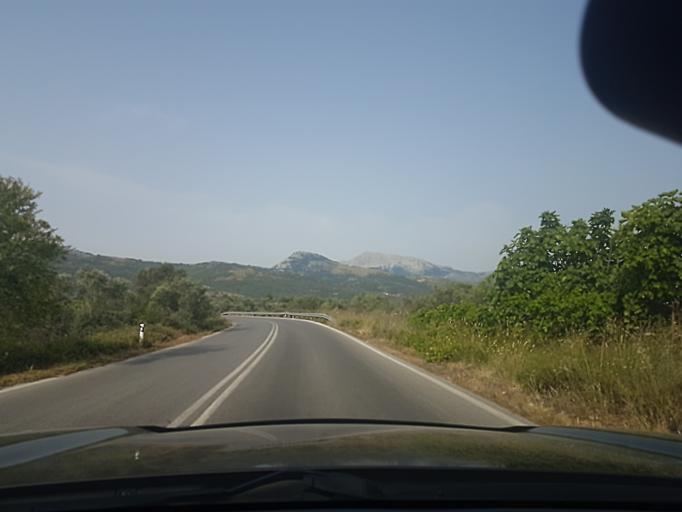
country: GR
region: Central Greece
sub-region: Nomos Evvoias
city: Yimnon
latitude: 38.5727
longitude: 23.8001
